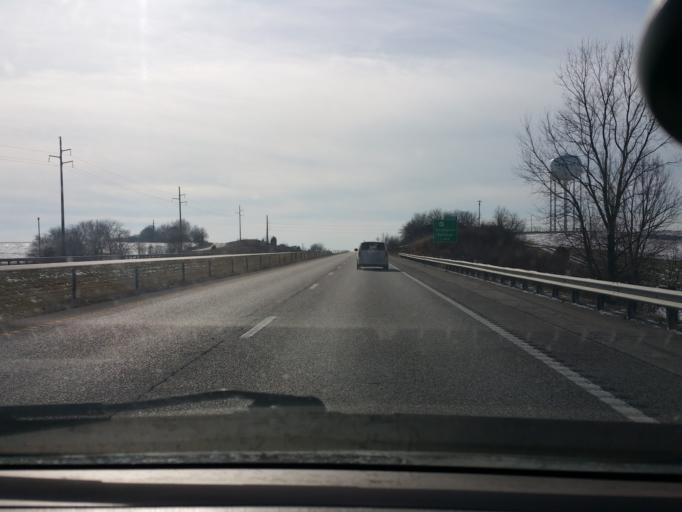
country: US
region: Missouri
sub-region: Clay County
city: Liberty
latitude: 39.3046
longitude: -94.4065
